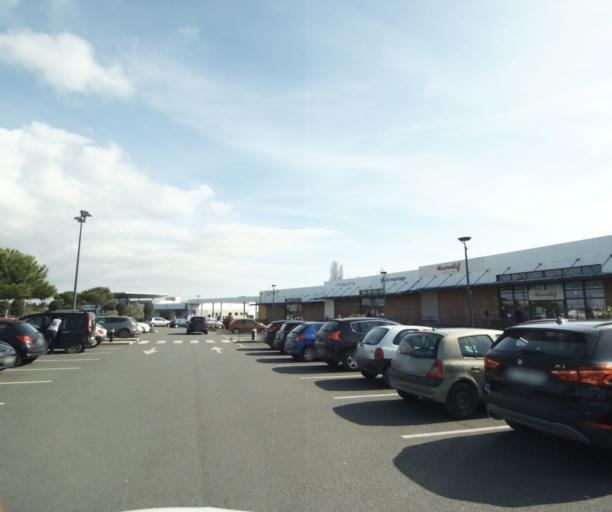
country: FR
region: Poitou-Charentes
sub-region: Departement de la Charente-Maritime
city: La Rochelle
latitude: 46.1726
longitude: -1.1683
